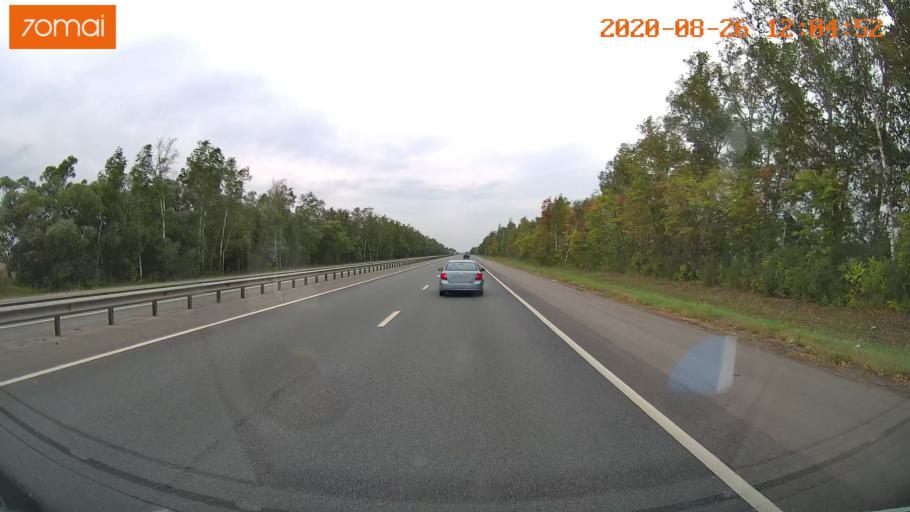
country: RU
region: Rjazan
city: Kiritsy
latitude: 54.3151
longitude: 40.1790
